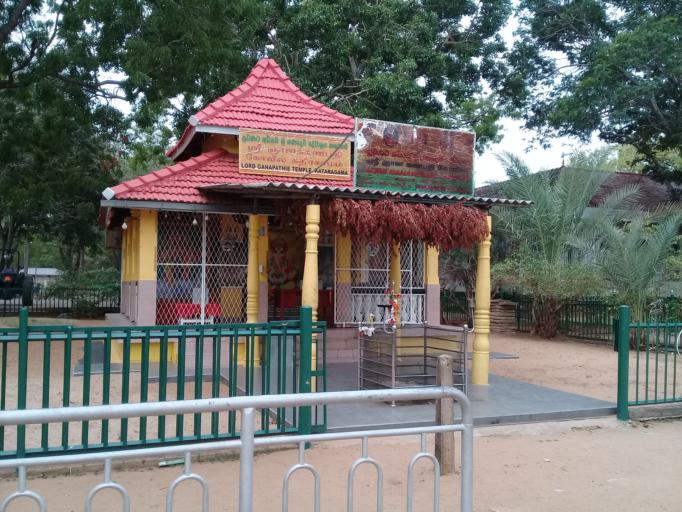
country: LK
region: Uva
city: Wattegama
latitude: 6.4181
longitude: 81.3341
